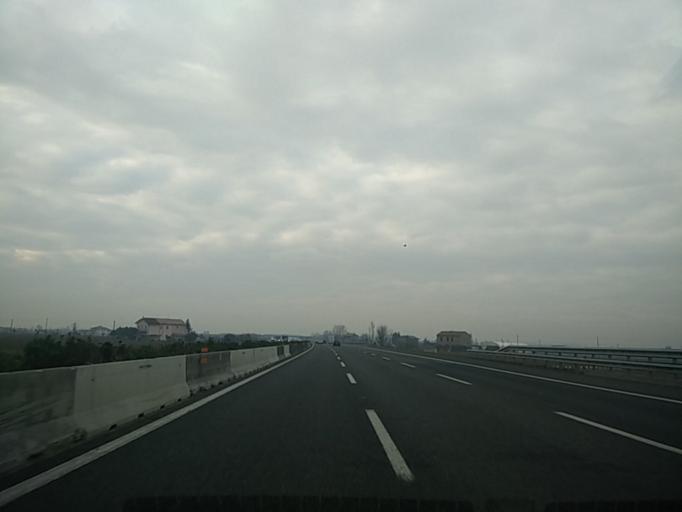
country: IT
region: Emilia-Romagna
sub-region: Forli-Cesena
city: San Mauro Pascoli
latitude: 44.0983
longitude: 12.4456
